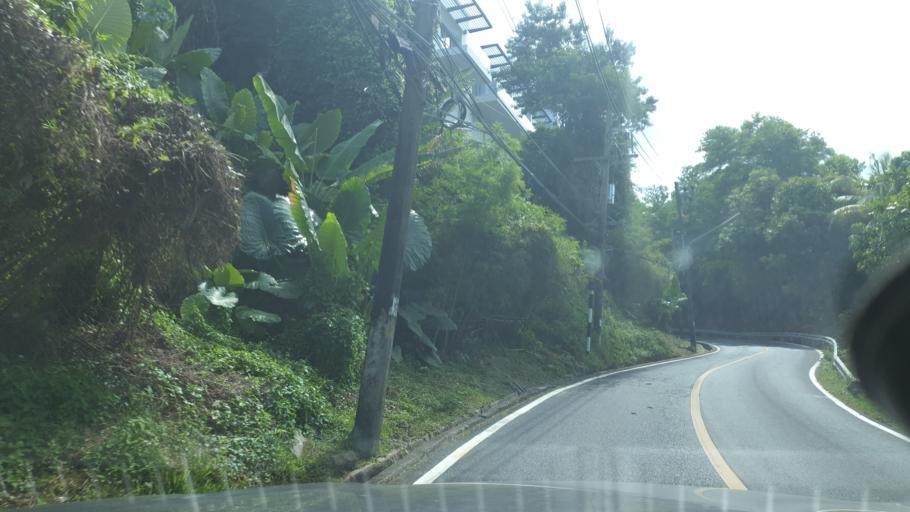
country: TH
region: Phuket
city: Thalang
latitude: 8.0528
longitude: 98.2779
